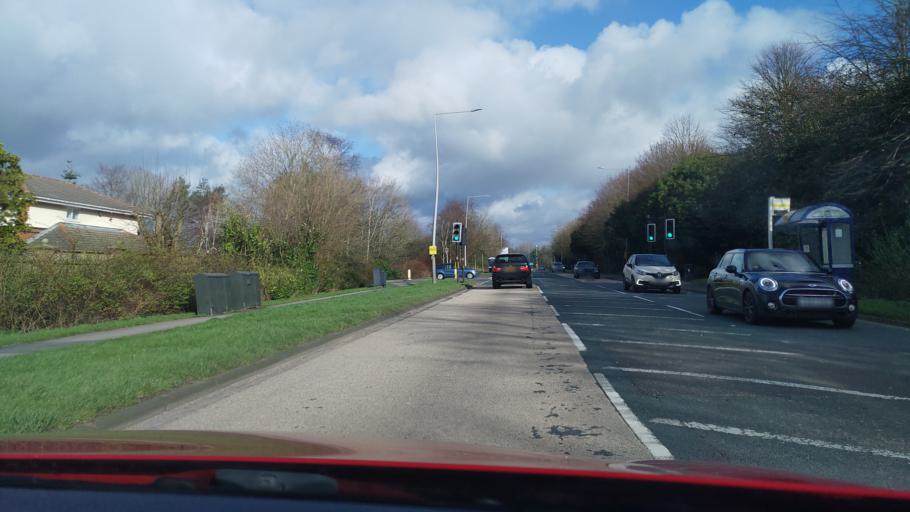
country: GB
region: England
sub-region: Lancashire
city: Goosnargh
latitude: 53.7880
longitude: -2.6693
